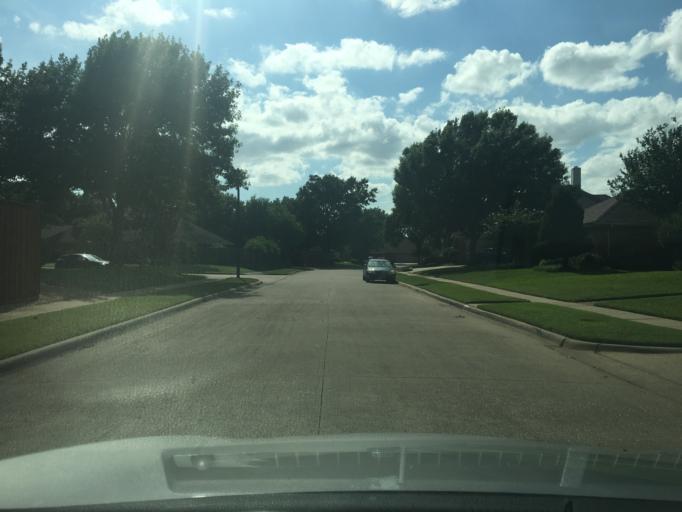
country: US
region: Texas
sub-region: Dallas County
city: Garland
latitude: 32.9355
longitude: -96.6744
